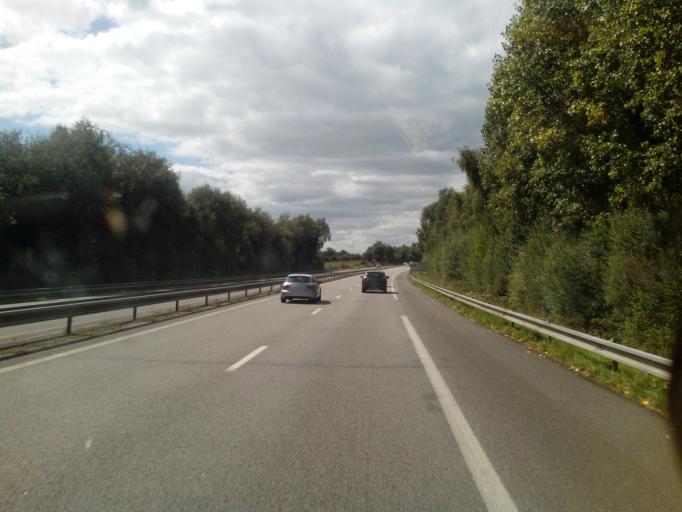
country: FR
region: Brittany
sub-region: Departement du Morbihan
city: Guenin
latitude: 47.8923
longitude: -2.9918
